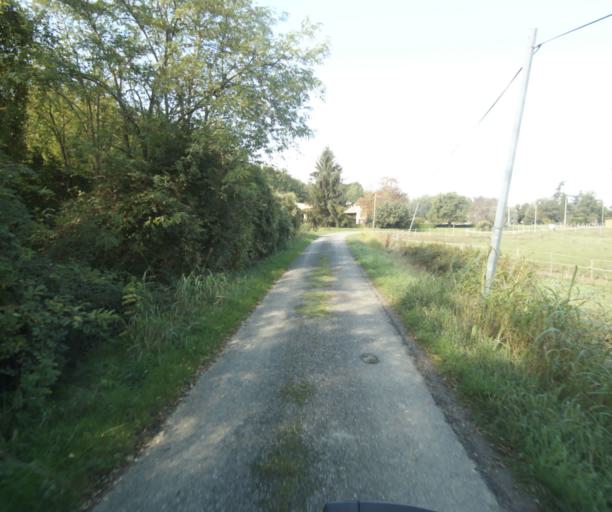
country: FR
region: Midi-Pyrenees
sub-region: Departement du Tarn-et-Garonne
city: Verdun-sur-Garonne
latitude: 43.8791
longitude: 1.2247
